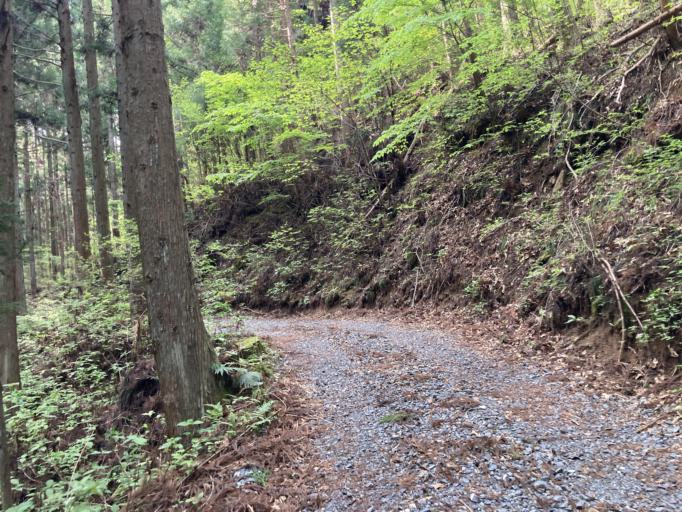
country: JP
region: Fukushima
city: Iwaki
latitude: 37.1643
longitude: 140.8027
